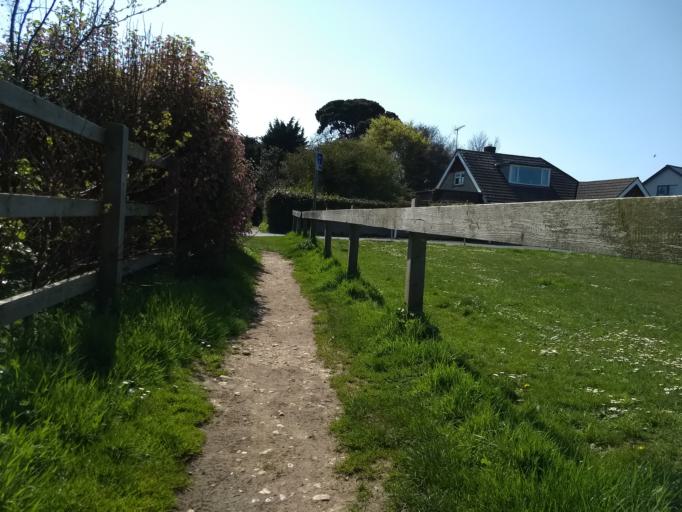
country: GB
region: England
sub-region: Isle of Wight
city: Bembridge
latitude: 50.6876
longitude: -1.0710
